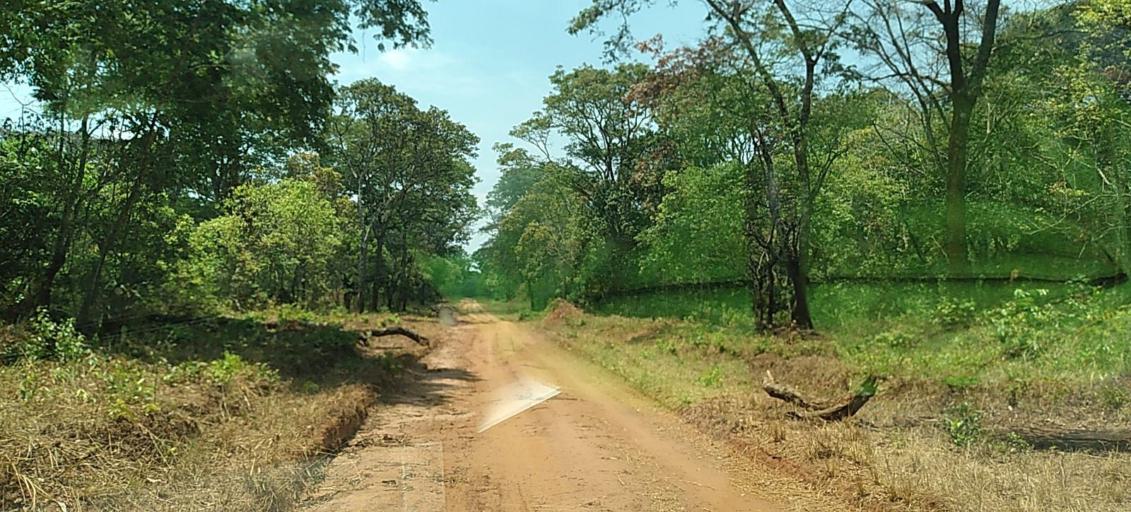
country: CD
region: Katanga
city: Kolwezi
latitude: -11.3530
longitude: 25.2119
